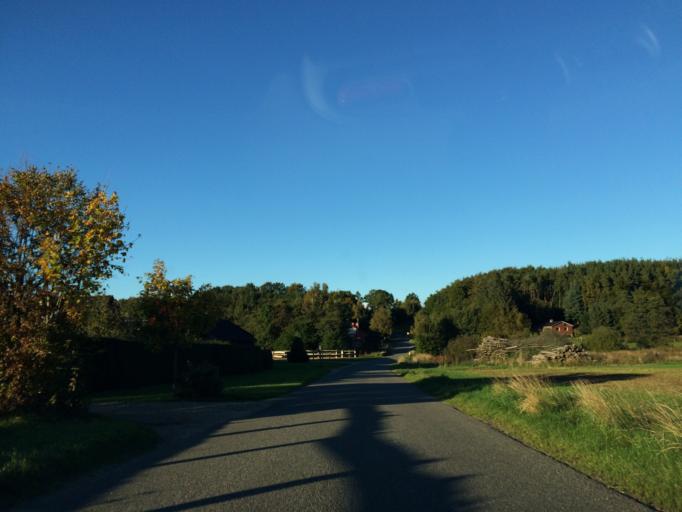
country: DK
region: Central Jutland
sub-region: Silkeborg Kommune
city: Svejbaek
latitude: 56.1572
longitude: 9.6915
